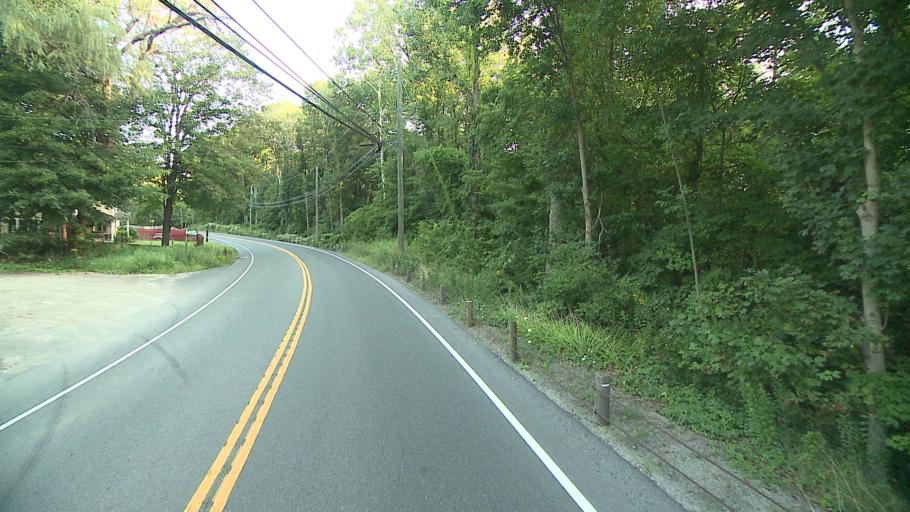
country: US
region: Connecticut
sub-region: Fairfield County
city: Sherman
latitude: 41.5989
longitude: -73.4577
